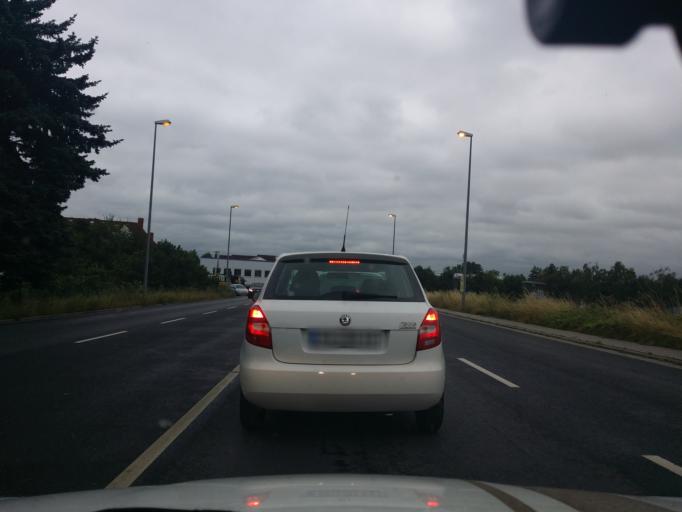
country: DE
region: Hesse
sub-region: Regierungsbezirk Darmstadt
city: Kriftel
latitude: 50.0904
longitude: 8.4626
